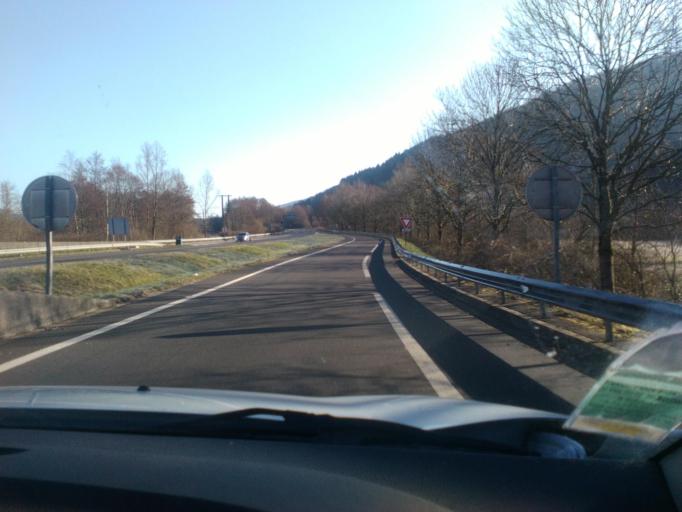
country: FR
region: Alsace
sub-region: Departement du Bas-Rhin
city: Russ
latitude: 48.4870
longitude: 7.2396
